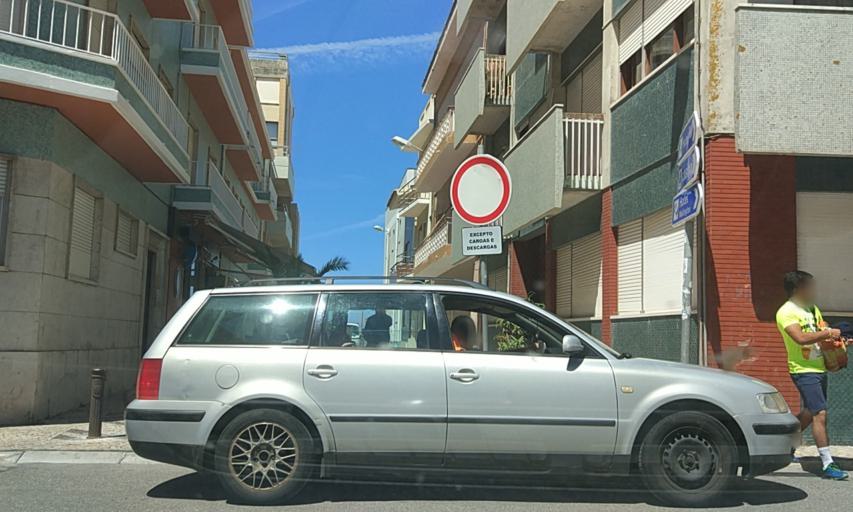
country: PT
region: Coimbra
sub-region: Figueira da Foz
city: Figueira da Foz
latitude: 40.1505
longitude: -8.8654
